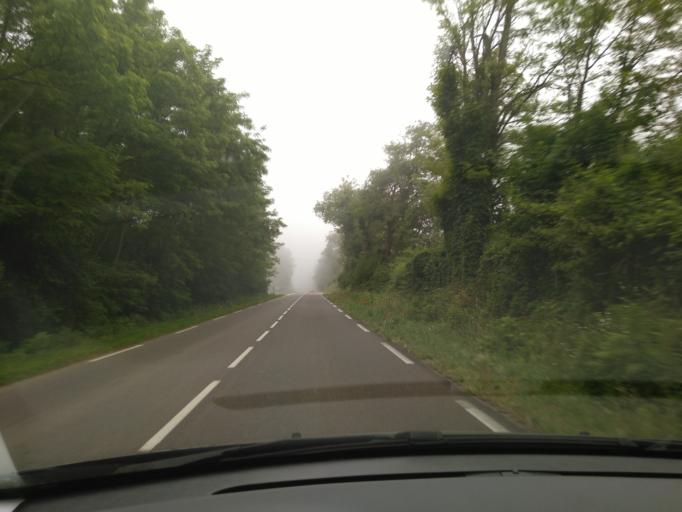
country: FR
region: Aquitaine
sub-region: Departement des Landes
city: Villeneuve-de-Marsan
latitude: 43.8847
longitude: -0.3698
